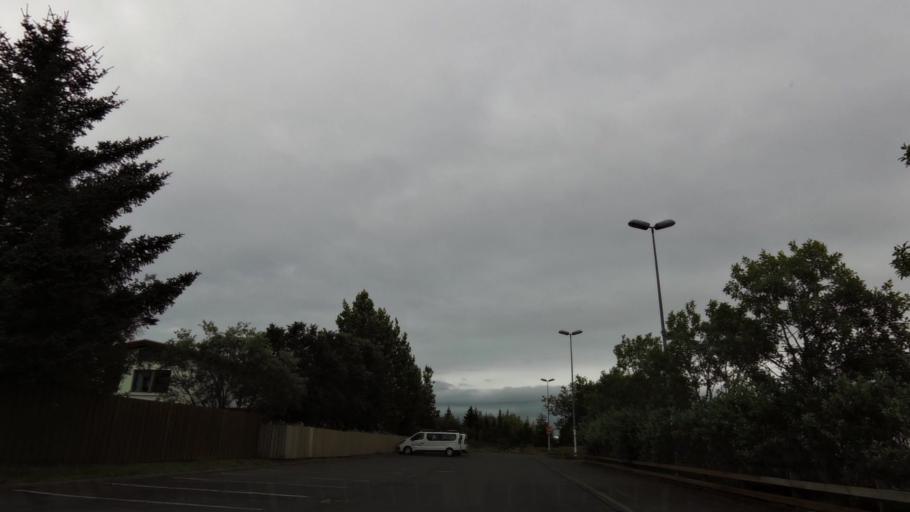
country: IS
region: Capital Region
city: Hafnarfjoerdur
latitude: 64.0819
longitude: -21.9577
